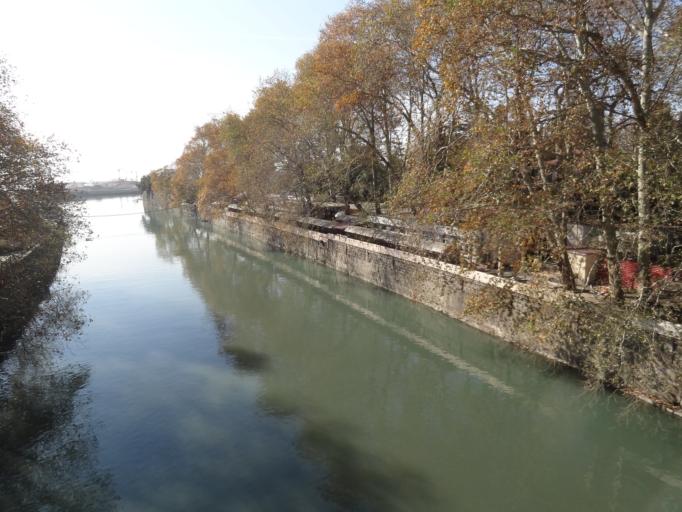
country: RU
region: Krasnodarskiy
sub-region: Sochi City
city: Sochi
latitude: 43.5871
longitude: 39.7161
